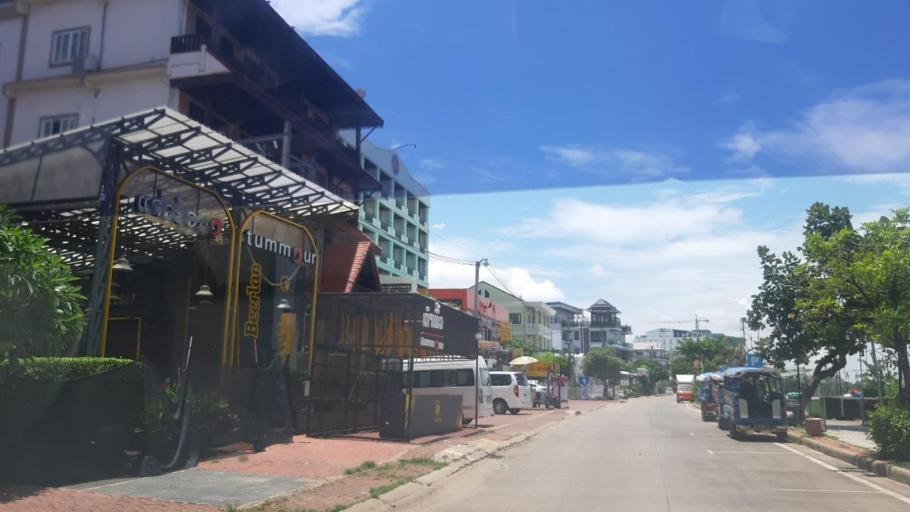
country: LA
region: Vientiane
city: Vientiane
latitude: 17.9664
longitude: 102.5933
